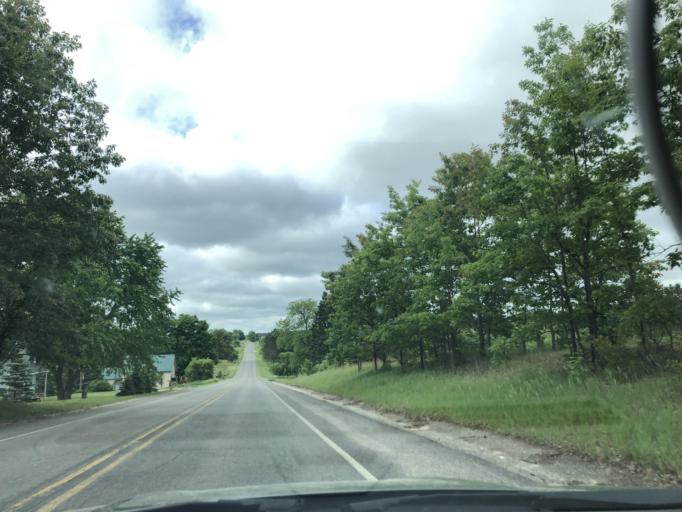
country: US
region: Michigan
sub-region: Missaukee County
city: Lake City
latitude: 44.4467
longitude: -85.2164
